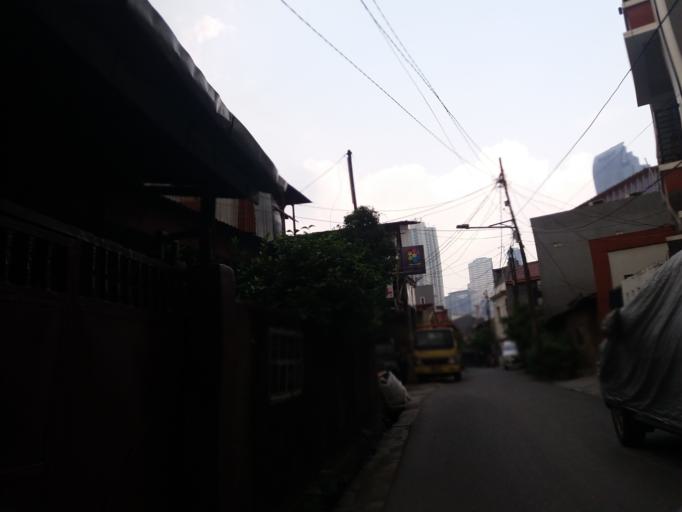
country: ID
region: Jakarta Raya
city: Jakarta
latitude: -6.2170
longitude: 106.8235
